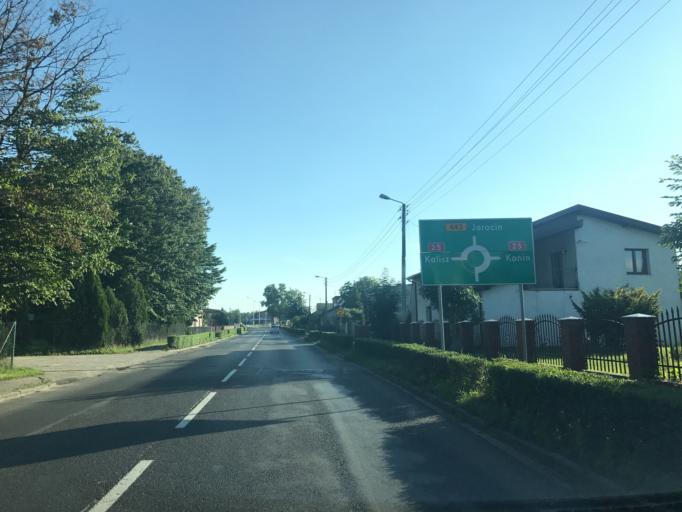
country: PL
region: Greater Poland Voivodeship
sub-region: Powiat koninski
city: Rychwal
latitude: 52.0693
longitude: 18.1645
